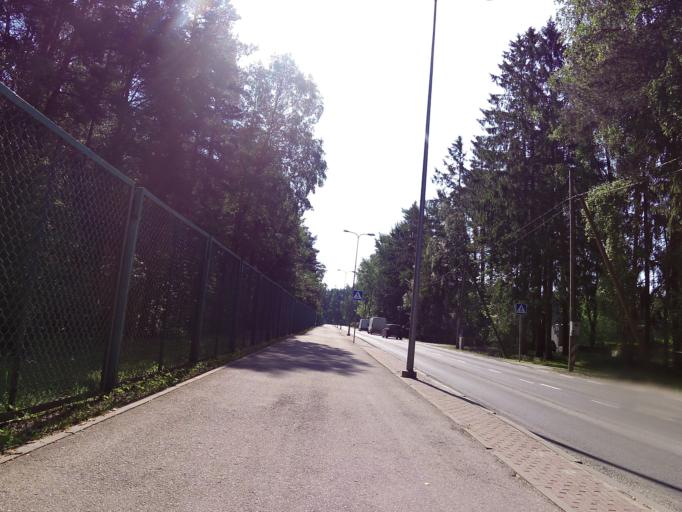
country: EE
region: Harju
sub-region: Saue vald
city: Laagri
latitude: 59.4325
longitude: 24.6334
